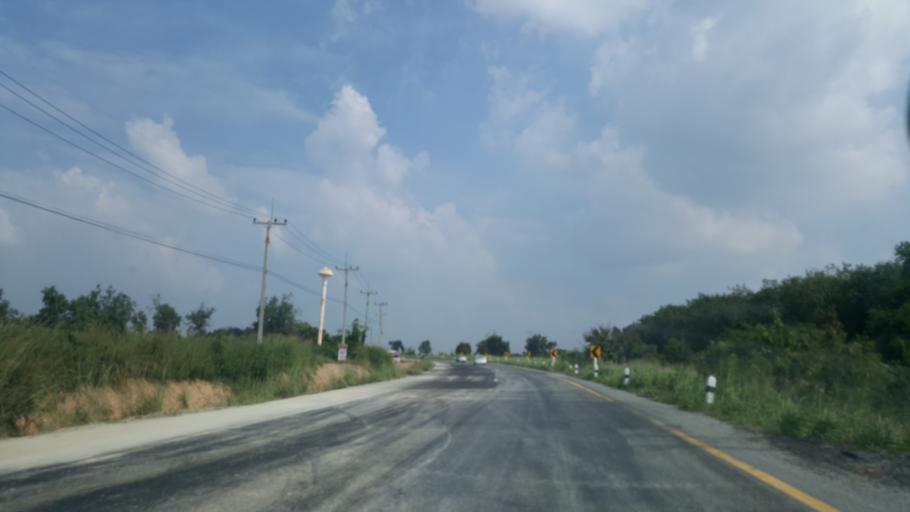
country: TH
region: Rayong
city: Ban Chang
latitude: 12.8613
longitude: 101.0237
